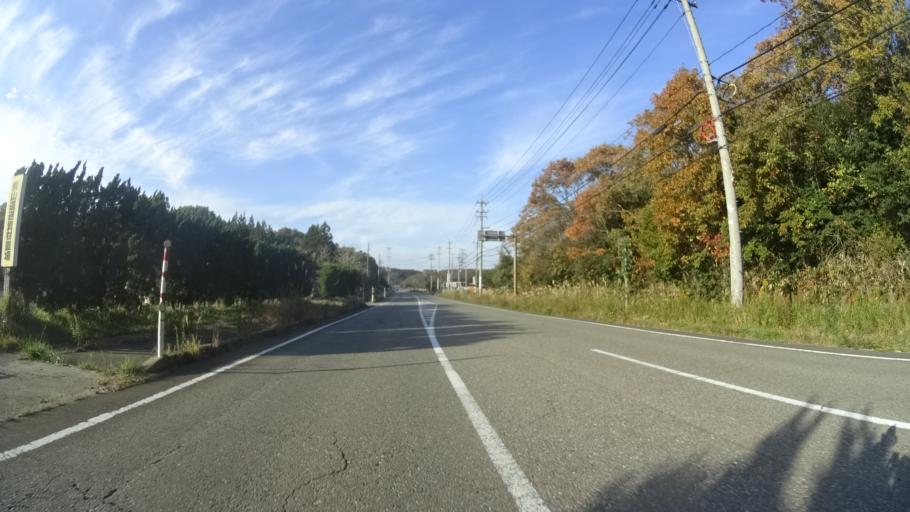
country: JP
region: Ishikawa
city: Hakui
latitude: 37.0396
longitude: 136.7783
